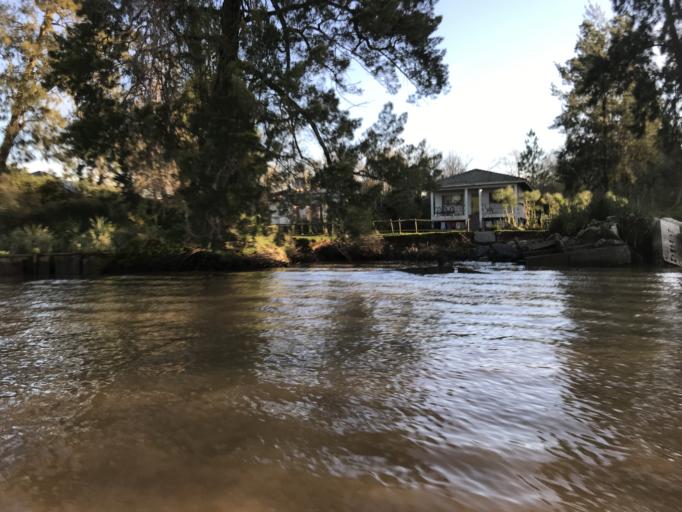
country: AR
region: Buenos Aires
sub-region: Partido de Tigre
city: Tigre
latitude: -34.3904
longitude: -58.5752
